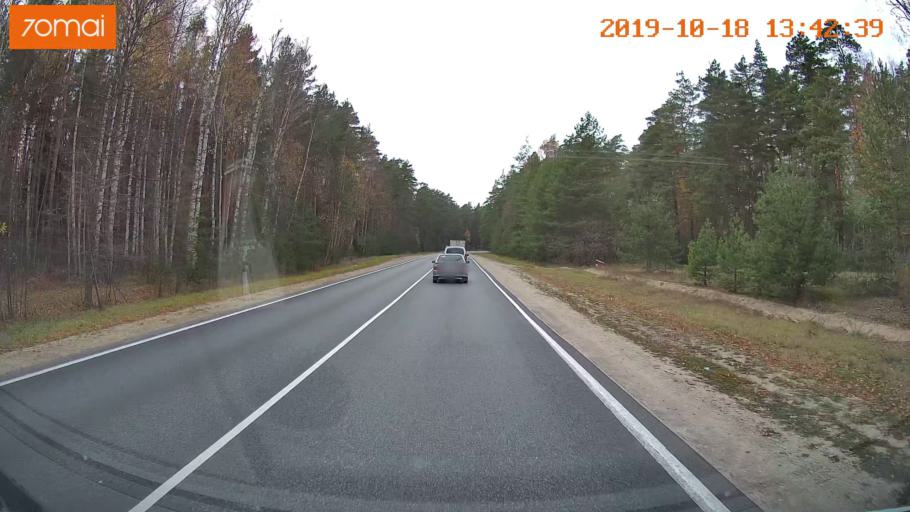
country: RU
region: Rjazan
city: Solotcha
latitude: 54.9271
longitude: 39.9856
